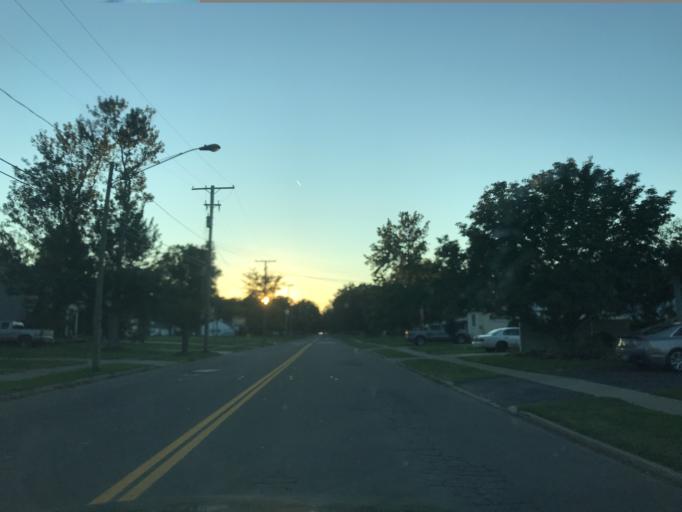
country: US
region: Ohio
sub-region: Ashtabula County
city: Ashtabula
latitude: 41.8925
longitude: -80.8136
